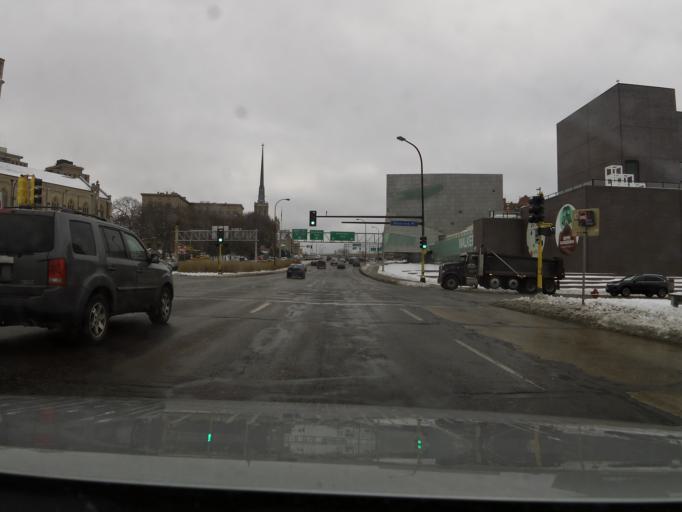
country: US
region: Minnesota
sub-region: Hennepin County
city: Minneapolis
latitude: 44.9693
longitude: -93.2881
